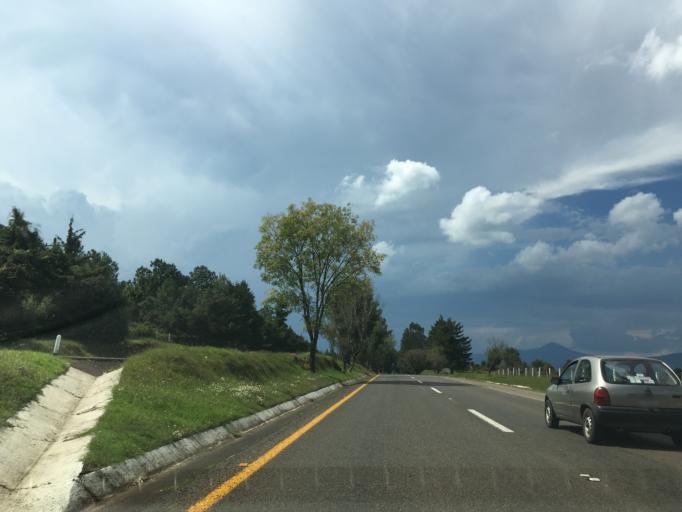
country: MX
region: Michoacan
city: Patzcuaro
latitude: 19.5338
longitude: -101.5678
